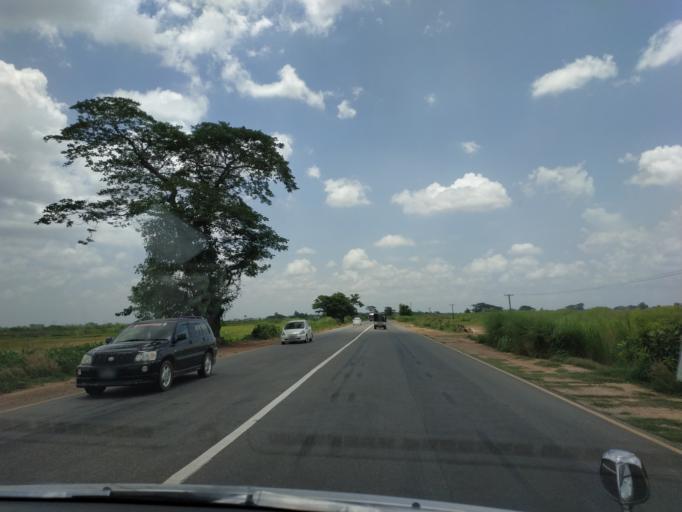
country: MM
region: Bago
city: Bago
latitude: 17.4695
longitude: 96.5622
